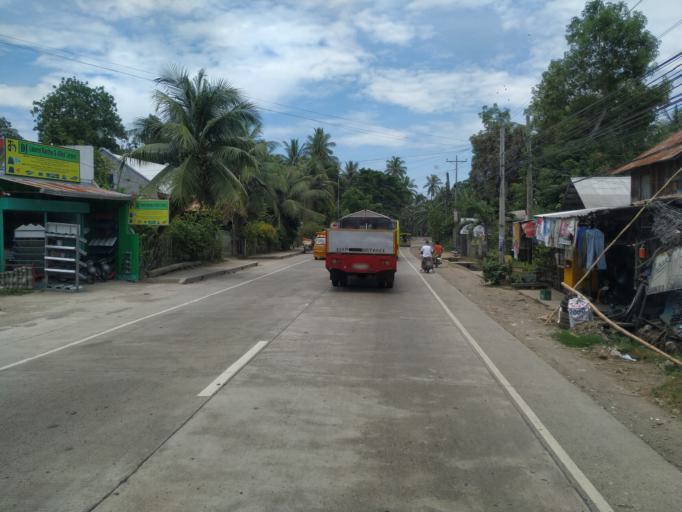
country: PH
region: Central Visayas
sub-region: Province of Negros Oriental
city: Sibulan
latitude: 9.3518
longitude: 123.2849
